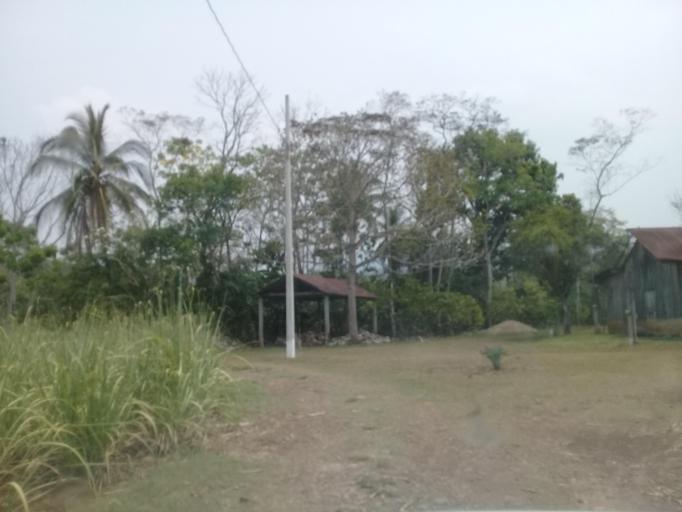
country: MX
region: Veracruz
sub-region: Tezonapa
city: Laguna Chica (Pueblo Nuevo)
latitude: 18.5061
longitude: -96.7074
